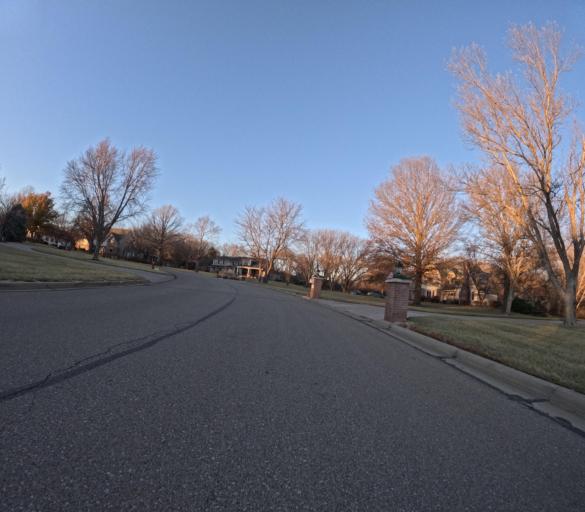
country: US
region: Kansas
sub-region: Riley County
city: Manhattan
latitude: 39.1952
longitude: -96.6313
